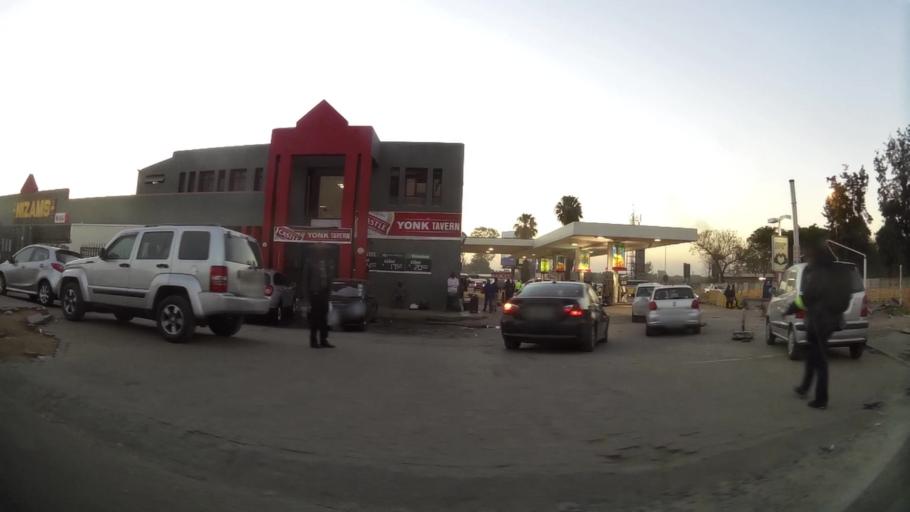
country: ZA
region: North-West
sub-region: Bojanala Platinum District Municipality
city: Rustenburg
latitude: -25.6617
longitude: 27.2389
